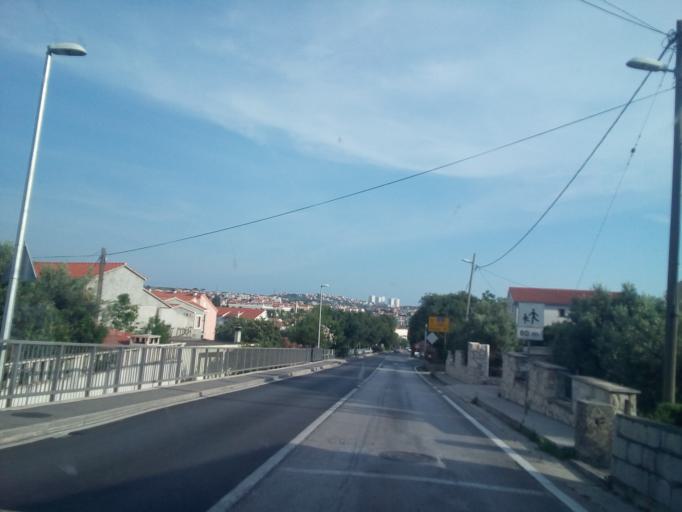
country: HR
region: Splitsko-Dalmatinska
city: Solin
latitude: 43.5439
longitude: 16.4915
